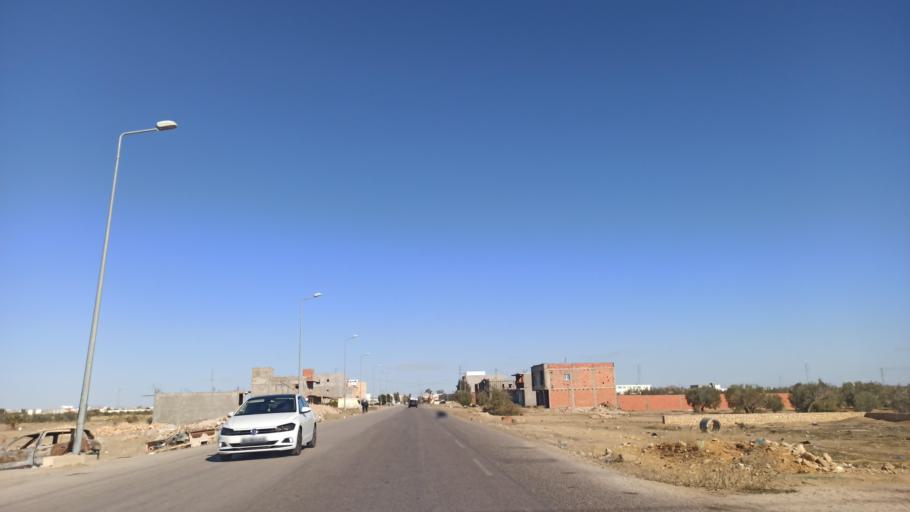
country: TN
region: Sidi Bu Zayd
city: Jilma
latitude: 35.2631
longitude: 9.4087
